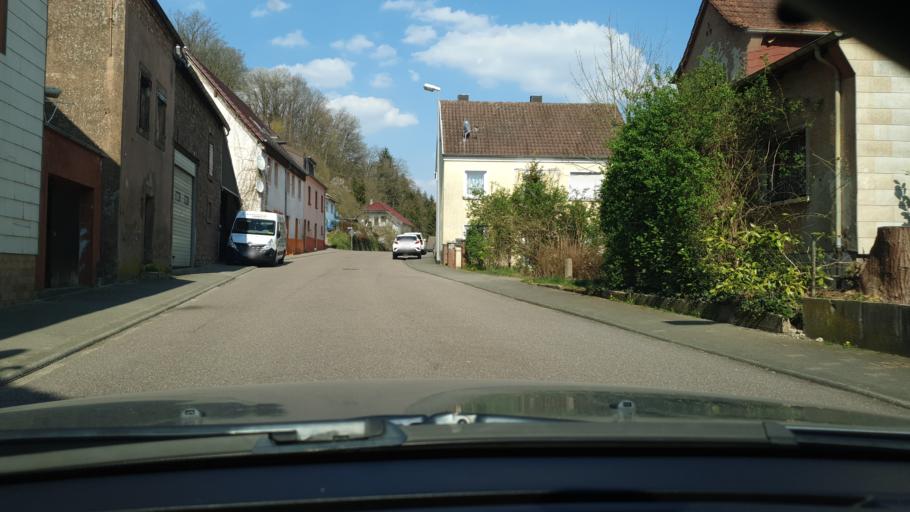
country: DE
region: Rheinland-Pfalz
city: Grossbundenbach
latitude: 49.2779
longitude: 7.4227
